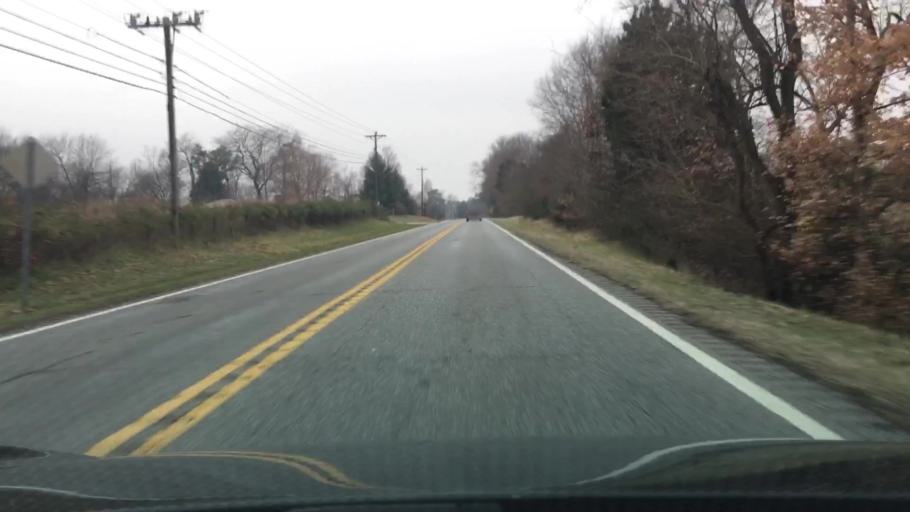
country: US
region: Kentucky
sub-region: Livingston County
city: Ledbetter
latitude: 36.9666
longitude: -88.4450
